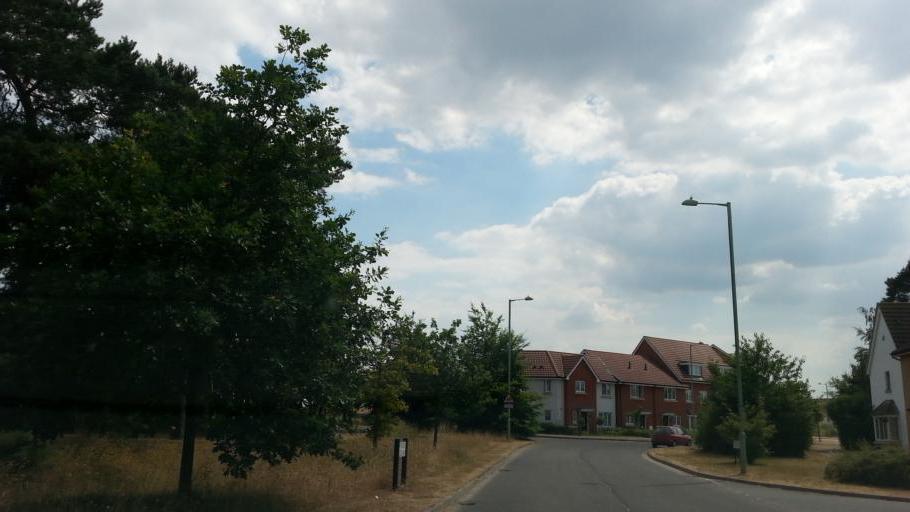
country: GB
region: England
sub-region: Cambridgeshire
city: Isleham
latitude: 52.3072
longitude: 0.4980
